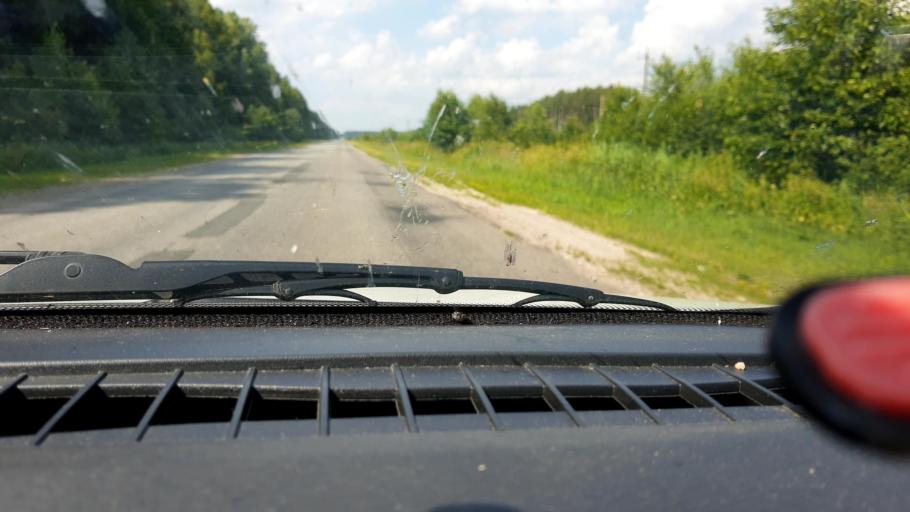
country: RU
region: Nizjnij Novgorod
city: Prudy
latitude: 57.4505
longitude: 46.0515
